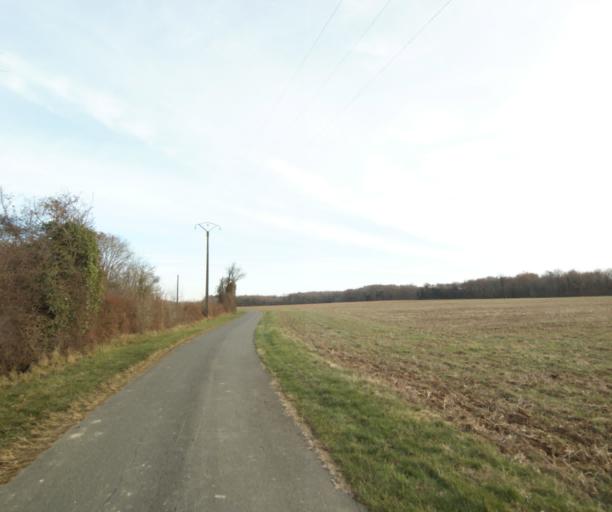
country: FR
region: Poitou-Charentes
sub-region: Departement de la Charente-Maritime
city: Saint-Hilaire-de-Villefranche
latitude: 45.8352
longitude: -0.5718
